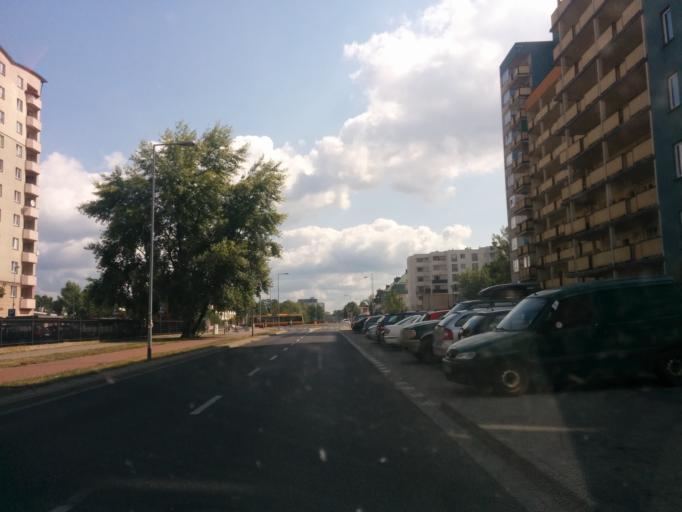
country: PL
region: Masovian Voivodeship
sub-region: Warszawa
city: Bialoleka
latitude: 52.3325
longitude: 20.9395
